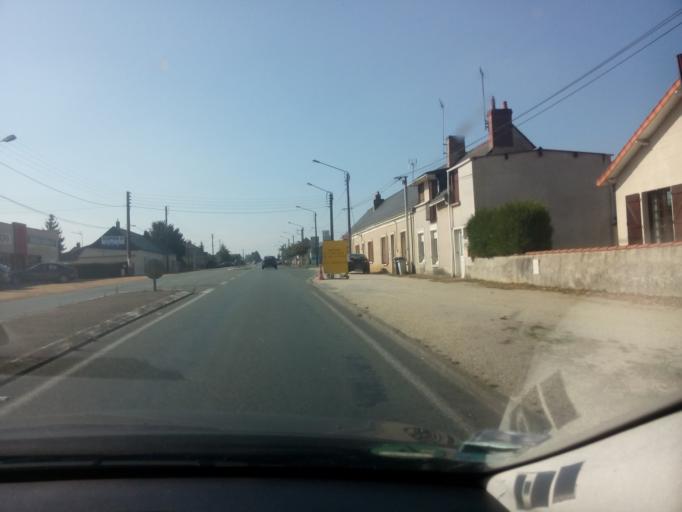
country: FR
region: Pays de la Loire
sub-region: Departement de Maine-et-Loire
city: Seiches-sur-le-Loir
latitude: 47.5705
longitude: -0.3582
